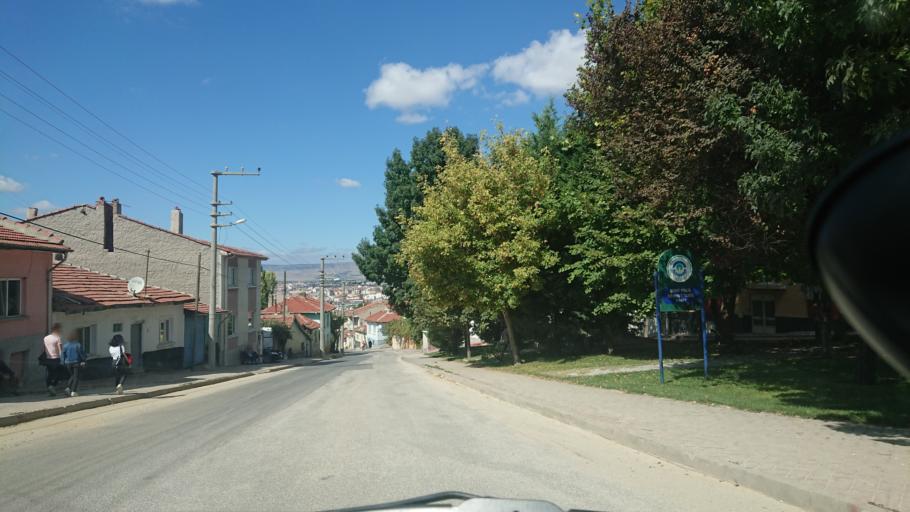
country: TR
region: Eskisehir
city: Eskisehir
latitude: 39.7594
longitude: 30.5298
